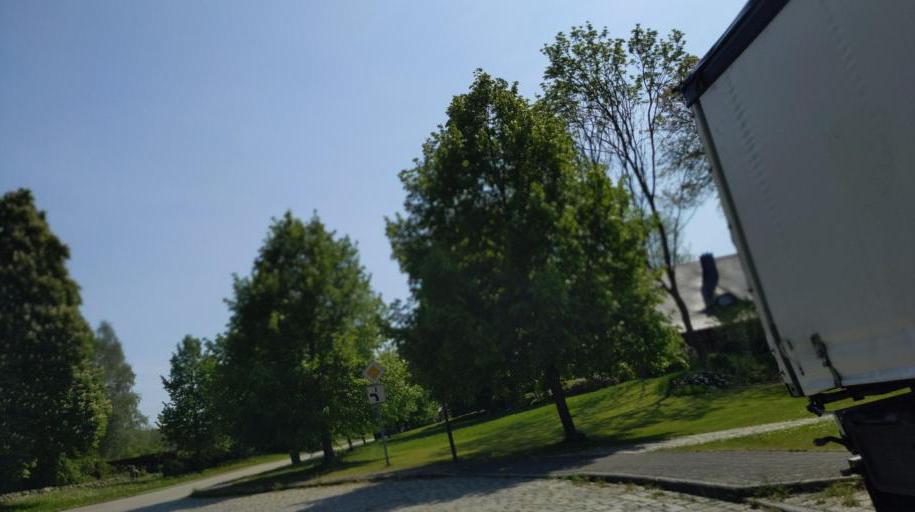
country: DE
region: Mecklenburg-Vorpommern
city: Selmsdorf
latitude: 53.8840
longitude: 10.8923
